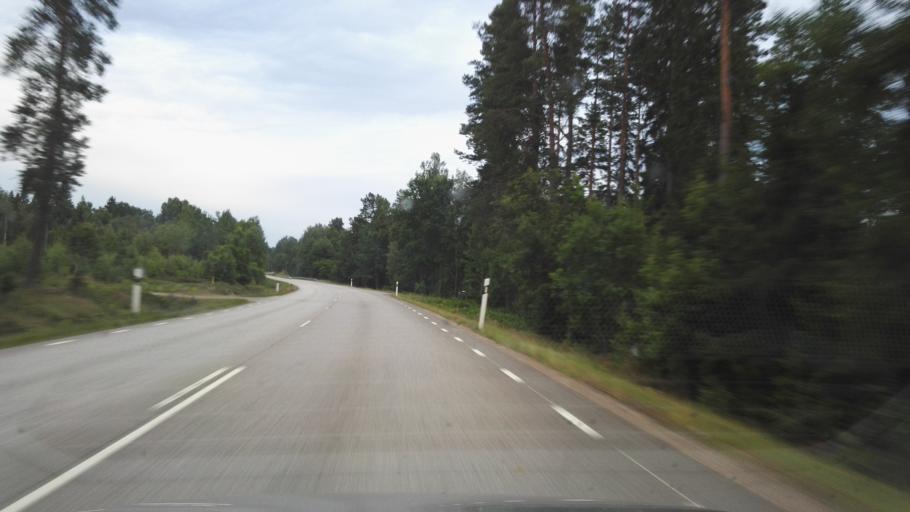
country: SE
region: Kronoberg
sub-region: Vaxjo Kommun
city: Braas
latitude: 57.0407
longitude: 15.0654
